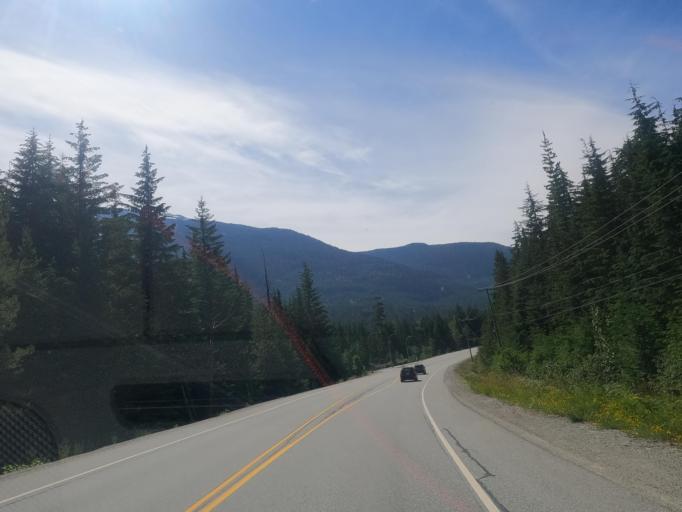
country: CA
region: British Columbia
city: Whistler
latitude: 50.1847
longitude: -122.8754
